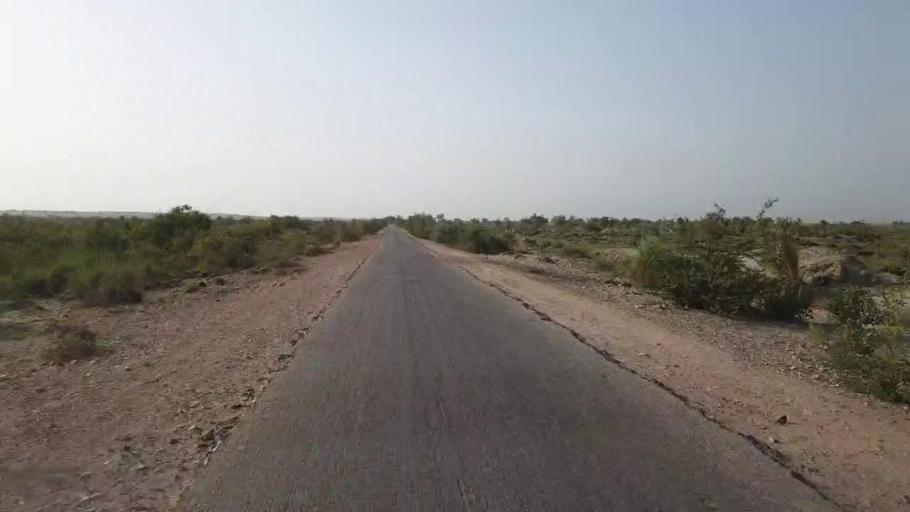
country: PK
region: Sindh
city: Jam Sahib
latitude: 26.4542
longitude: 68.8613
